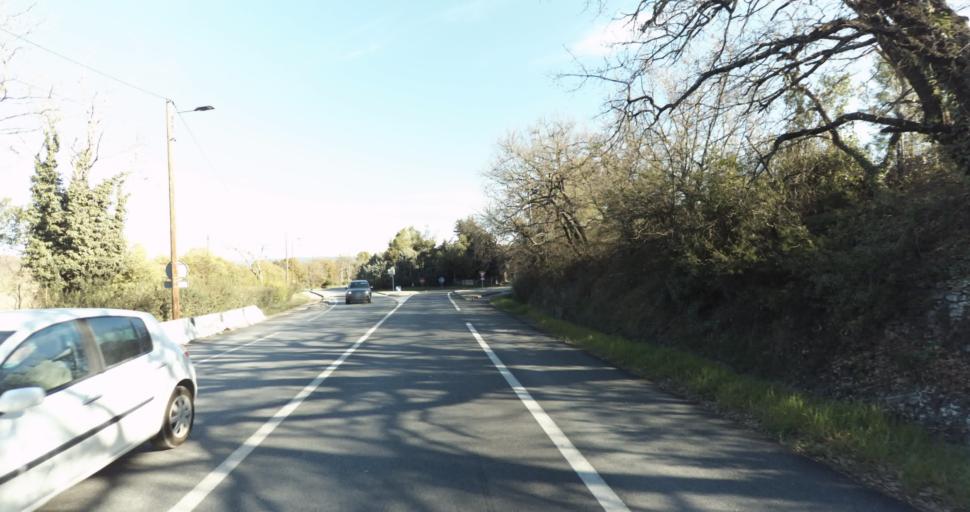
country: FR
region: Provence-Alpes-Cote d'Azur
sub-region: Departement des Bouches-du-Rhone
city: Aix-en-Provence
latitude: 43.5563
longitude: 5.4340
